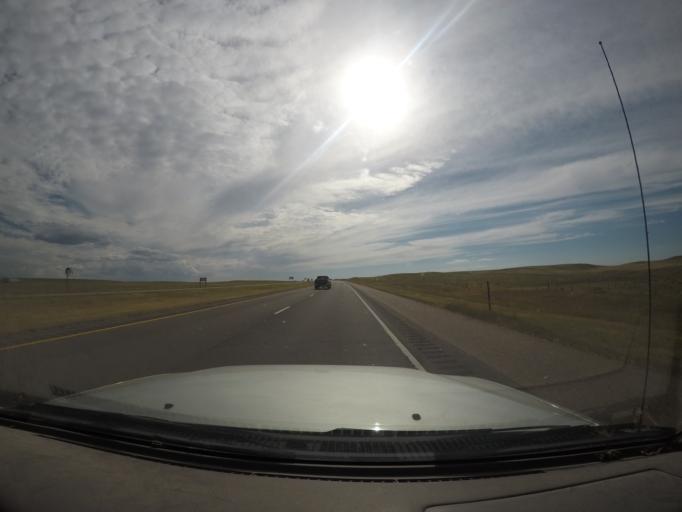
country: US
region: Nebraska
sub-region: Kimball County
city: Kimball
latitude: 41.2142
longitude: -103.6853
